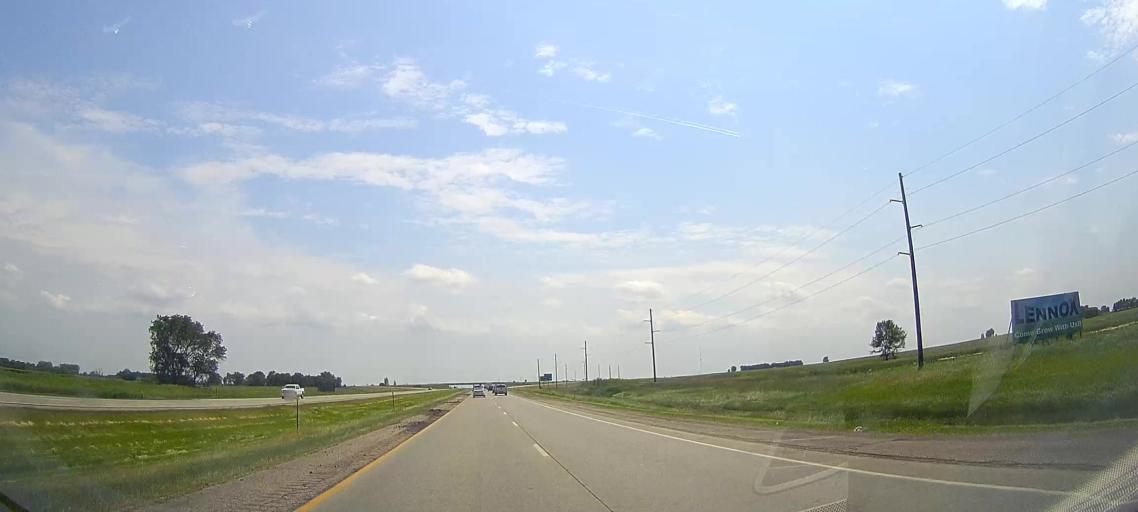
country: US
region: South Dakota
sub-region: Lincoln County
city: Tea
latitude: 43.3962
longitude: -96.7965
